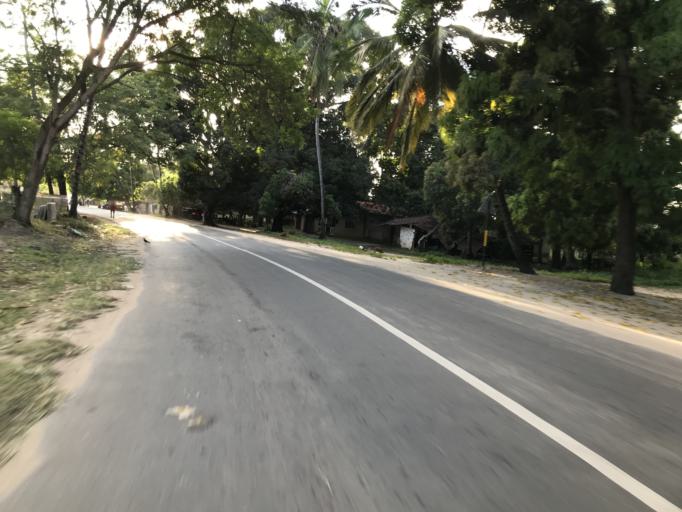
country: TZ
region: Dar es Salaam
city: Dar es Salaam
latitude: -6.8659
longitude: 39.3646
